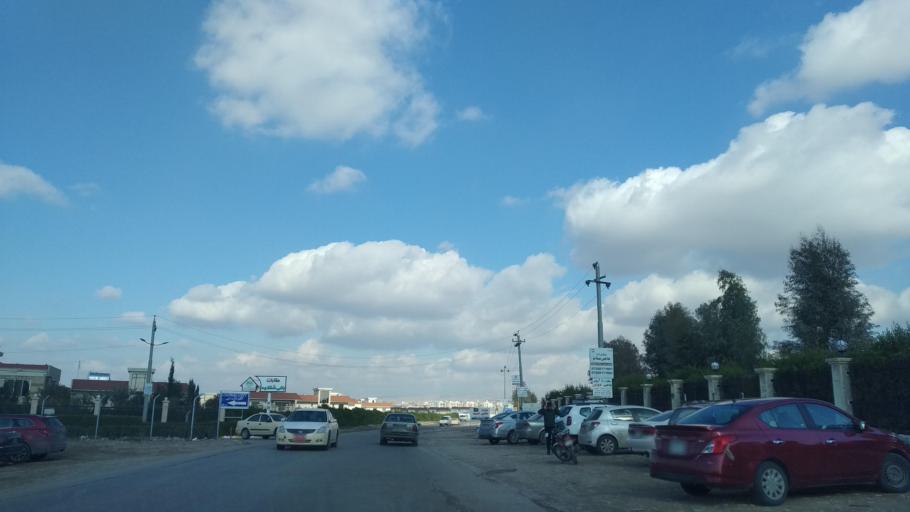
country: IQ
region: Arbil
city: Erbil
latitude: 36.2086
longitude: 44.1339
